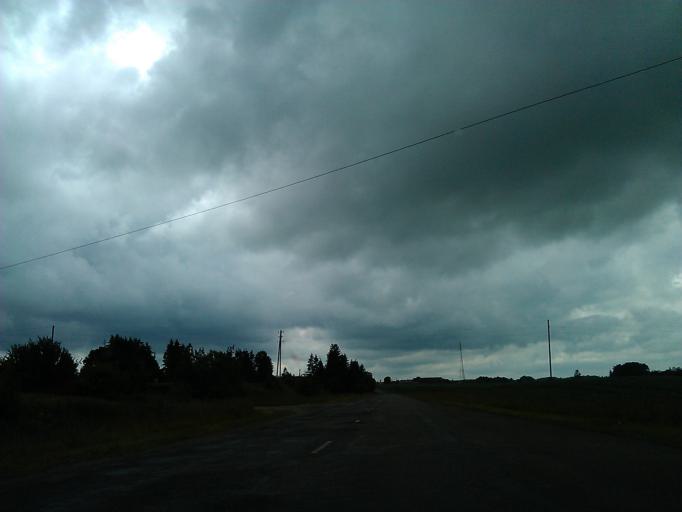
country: LV
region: Aizpute
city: Aizpute
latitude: 56.8451
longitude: 21.7773
